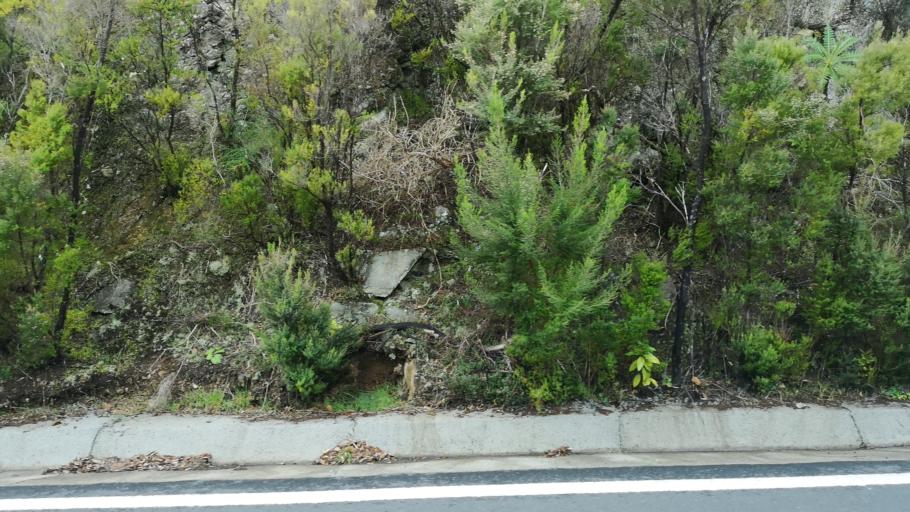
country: ES
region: Canary Islands
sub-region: Provincia de Santa Cruz de Tenerife
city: Alajero
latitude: 28.1137
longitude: -17.2422
